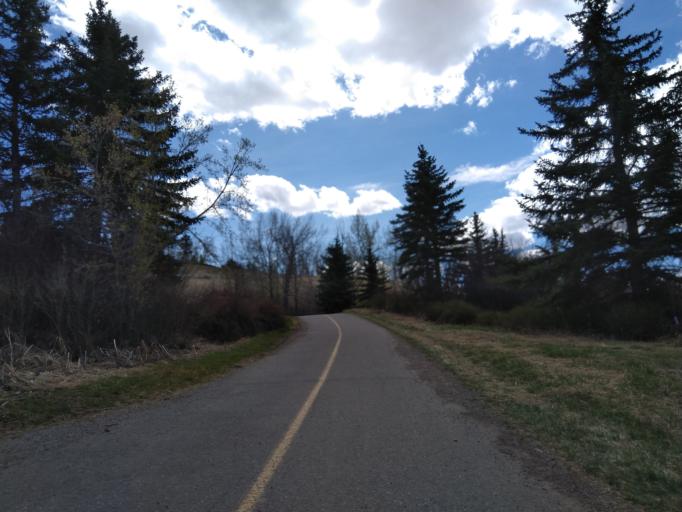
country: CA
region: Alberta
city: Calgary
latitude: 51.0836
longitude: -114.1652
